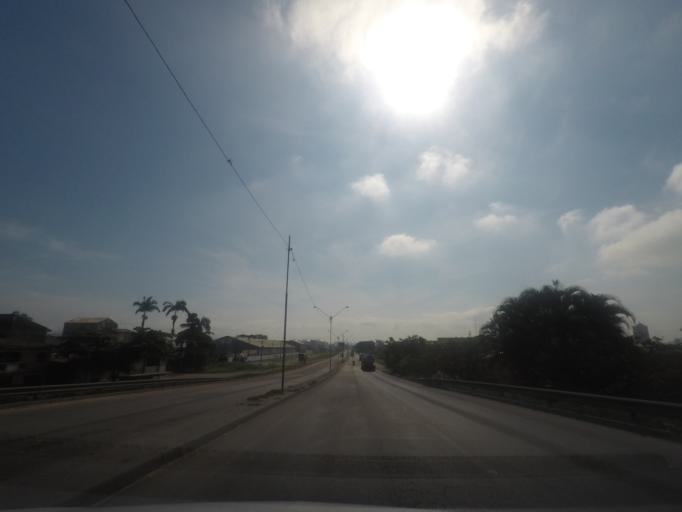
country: BR
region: Parana
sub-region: Paranagua
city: Paranagua
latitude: -25.5248
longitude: -48.5267
